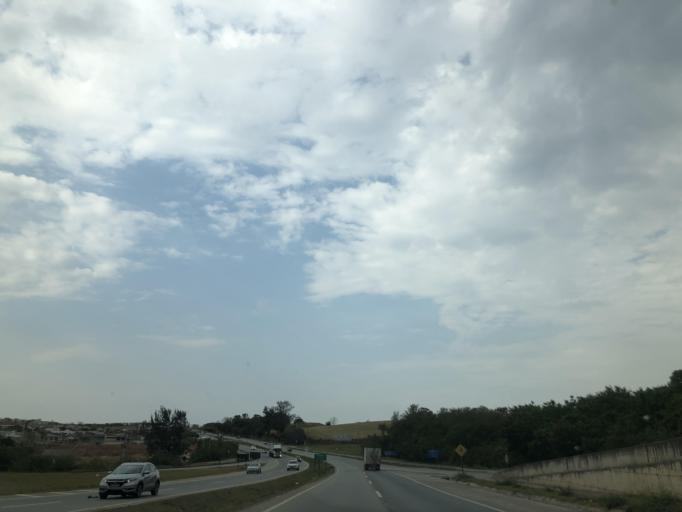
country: BR
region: Sao Paulo
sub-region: Votorantim
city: Votorantim
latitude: -23.5640
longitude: -47.4932
